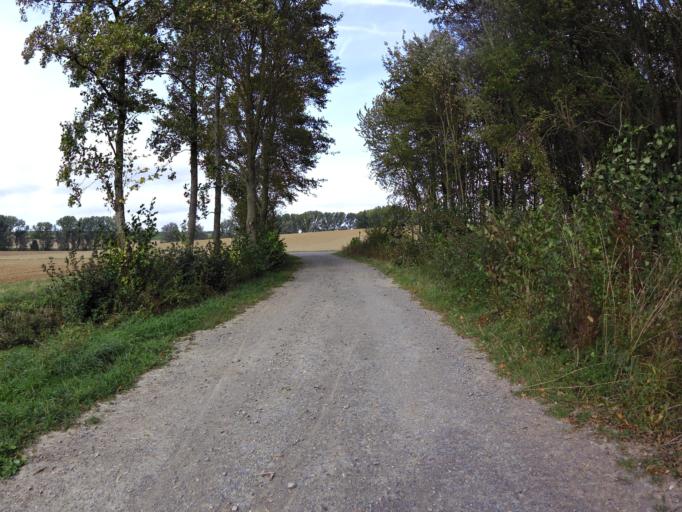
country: DE
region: Bavaria
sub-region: Regierungsbezirk Unterfranken
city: Reichenberg
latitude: 49.7035
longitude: 9.9509
